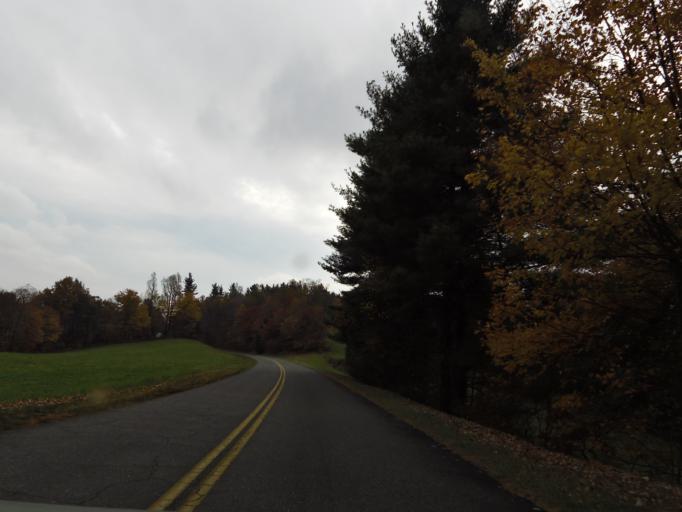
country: US
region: North Carolina
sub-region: Ashe County
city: West Jefferson
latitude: 36.2711
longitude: -81.4300
